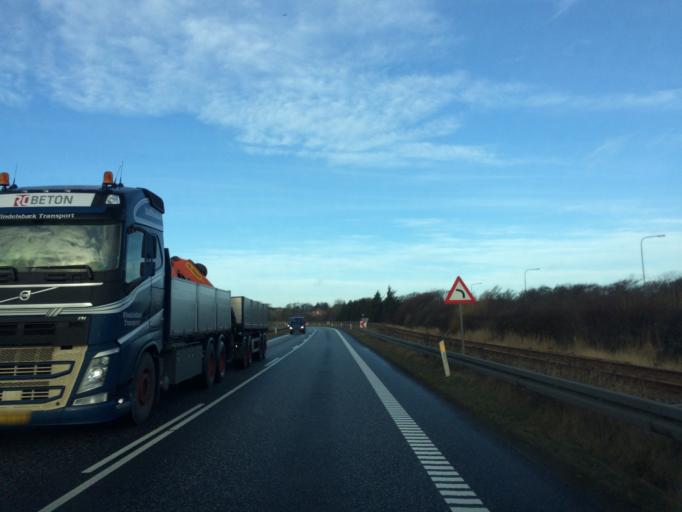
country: DK
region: Central Jutland
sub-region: Struer Kommune
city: Struer
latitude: 56.5006
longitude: 8.5818
